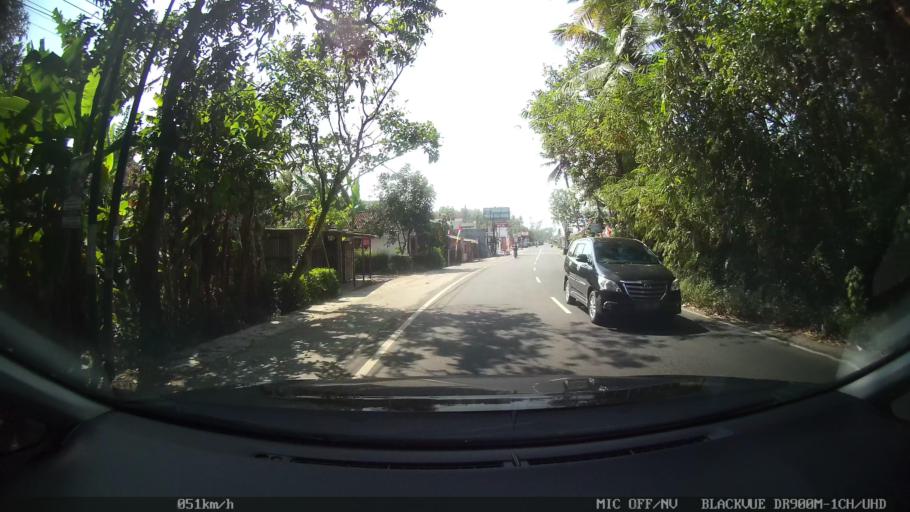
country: ID
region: Daerah Istimewa Yogyakarta
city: Srandakan
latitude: -7.9298
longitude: 110.2066
